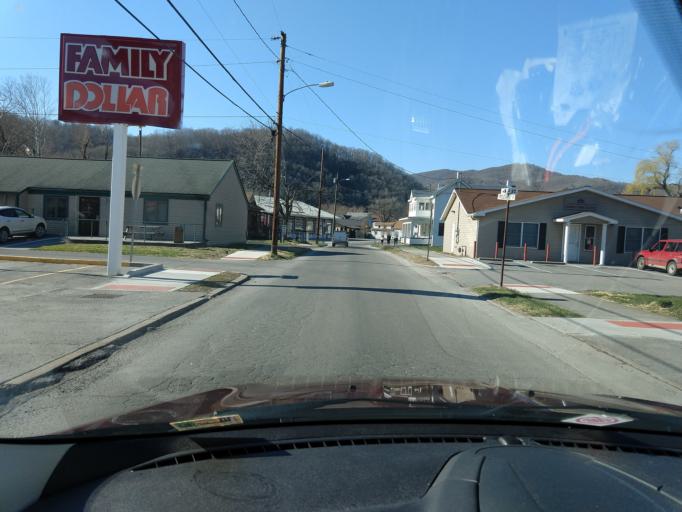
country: US
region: West Virginia
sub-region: Summers County
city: Hinton
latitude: 37.6614
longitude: -80.8922
